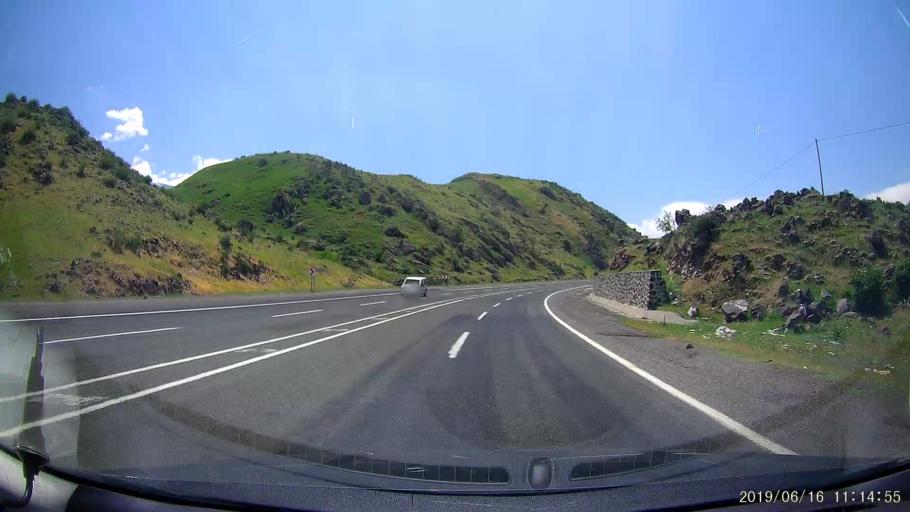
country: TR
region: Igdir
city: Igdir
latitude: 39.7717
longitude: 44.1432
